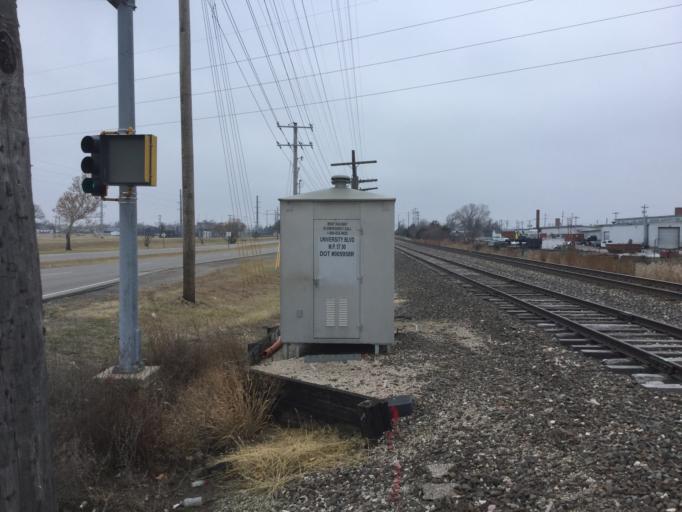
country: US
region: Kansas
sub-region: Shawnee County
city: Topeka
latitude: 38.9529
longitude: -95.6876
